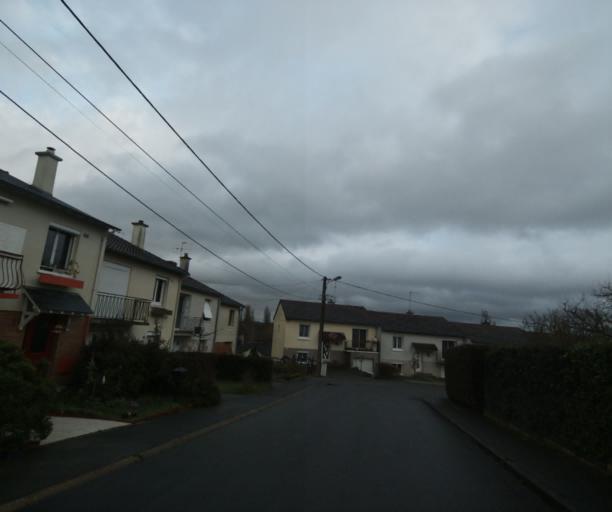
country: FR
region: Pays de la Loire
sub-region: Departement de la Sarthe
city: Coulaines
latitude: 48.0268
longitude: 0.1852
